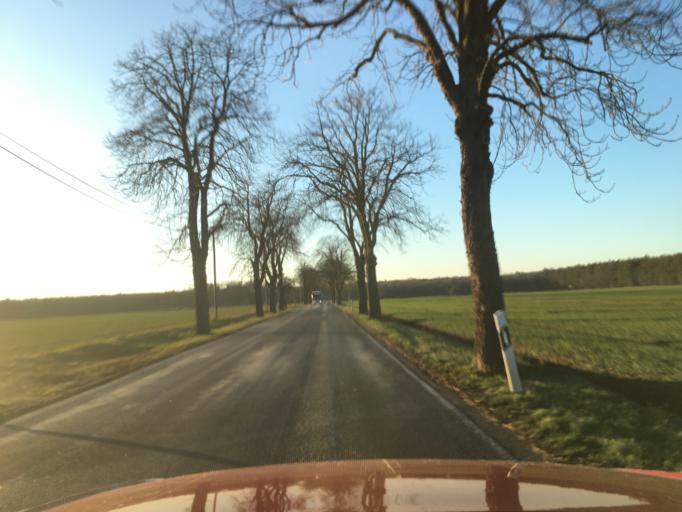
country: DE
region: Saxony-Anhalt
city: Klieken
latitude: 51.9243
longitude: 12.3140
